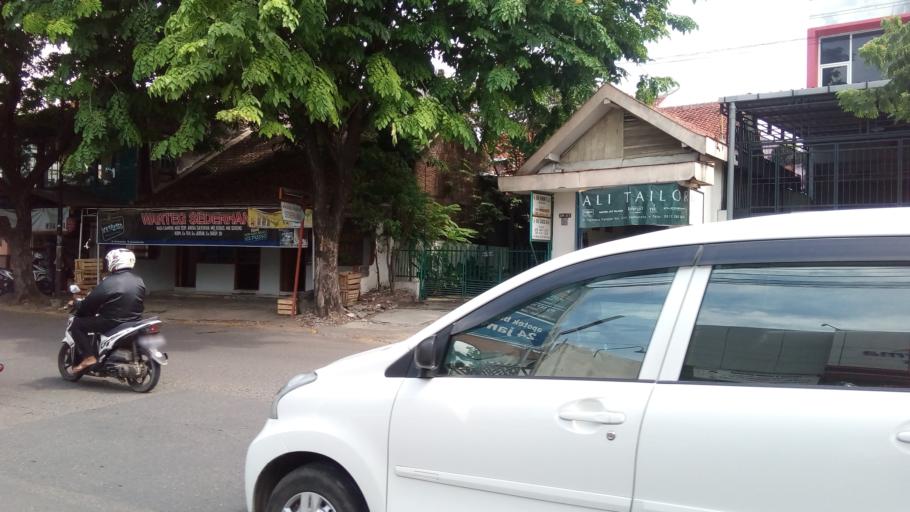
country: ID
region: Central Java
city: Semarang
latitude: -7.0092
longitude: 110.4339
